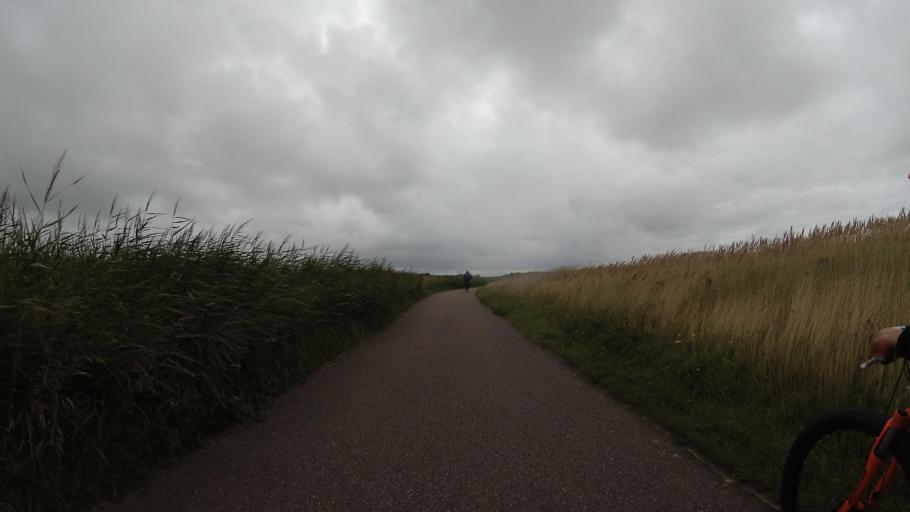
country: NL
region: North Holland
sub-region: Gemeente Den Helder
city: Den Helder
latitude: 52.9231
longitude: 4.7381
